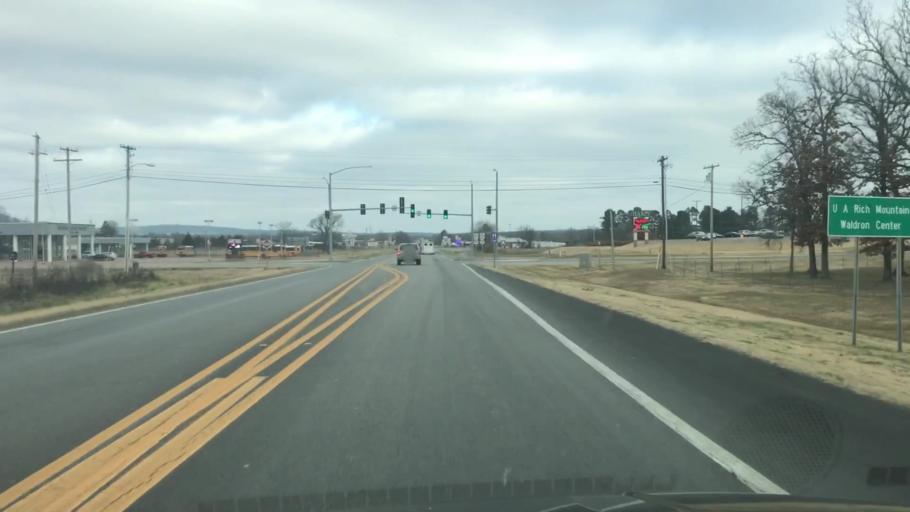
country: US
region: Arkansas
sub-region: Scott County
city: Waldron
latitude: 34.8958
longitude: -94.1076
